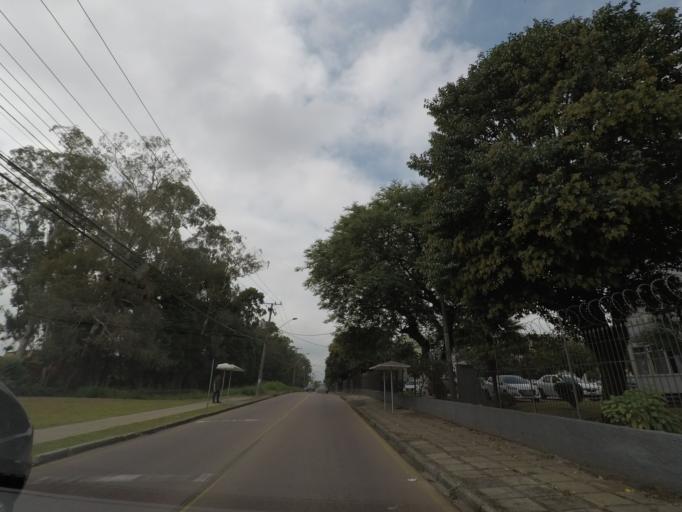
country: BR
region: Parana
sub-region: Curitiba
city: Curitiba
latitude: -25.4942
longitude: -49.3153
